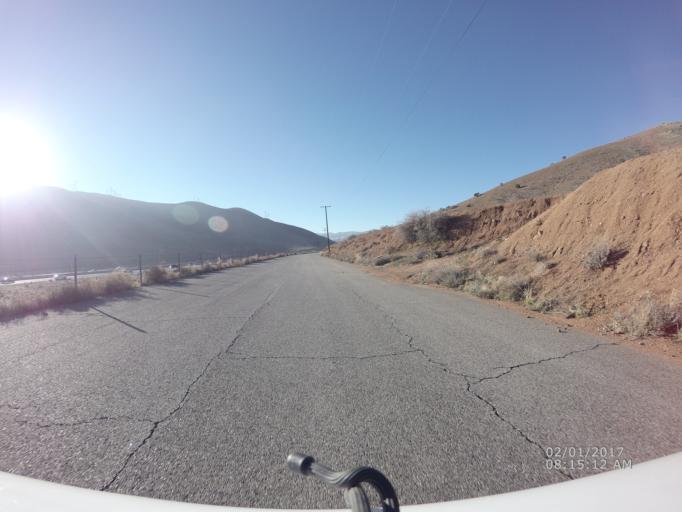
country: US
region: California
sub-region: Los Angeles County
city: Vincent
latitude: 34.5096
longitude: -118.1135
